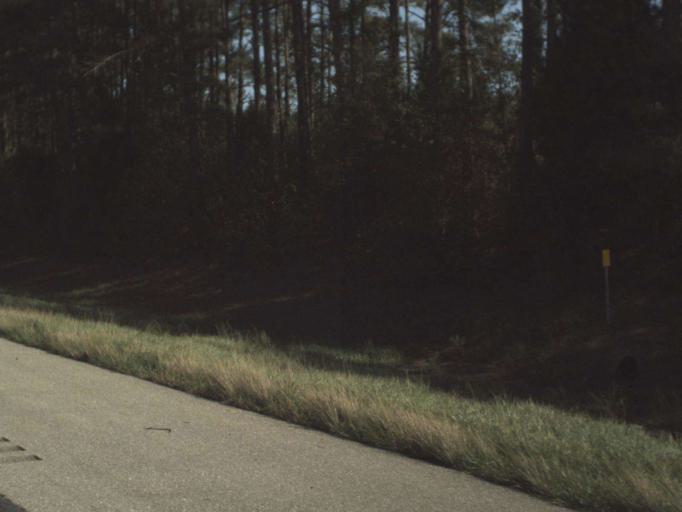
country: US
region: Florida
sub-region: Washington County
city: Chipley
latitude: 30.7464
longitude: -85.5348
